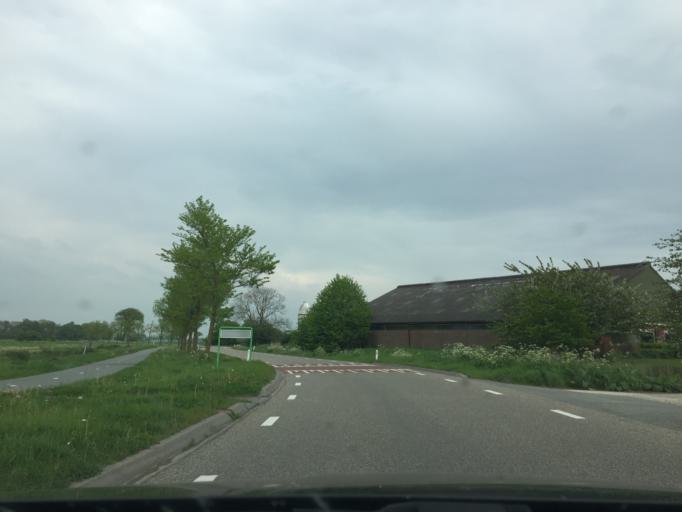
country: NL
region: Groningen
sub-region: Gemeente Zuidhorn
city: Aduard
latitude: 53.2659
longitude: 6.4410
